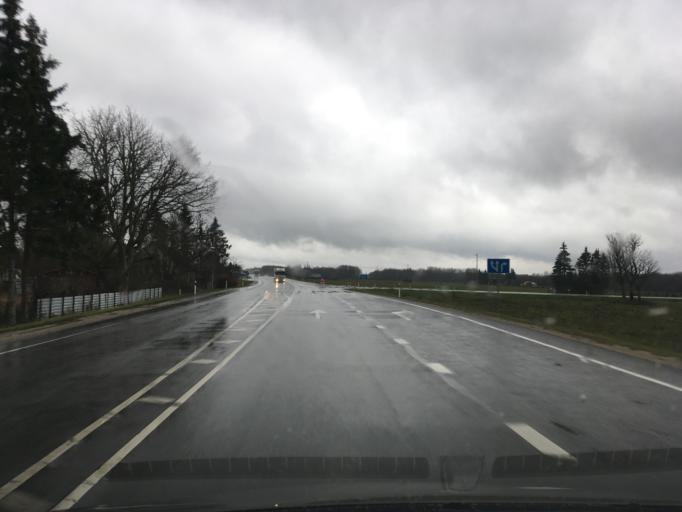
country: EE
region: Laeaene
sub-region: Lihula vald
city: Lihula
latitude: 58.7672
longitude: 23.9882
